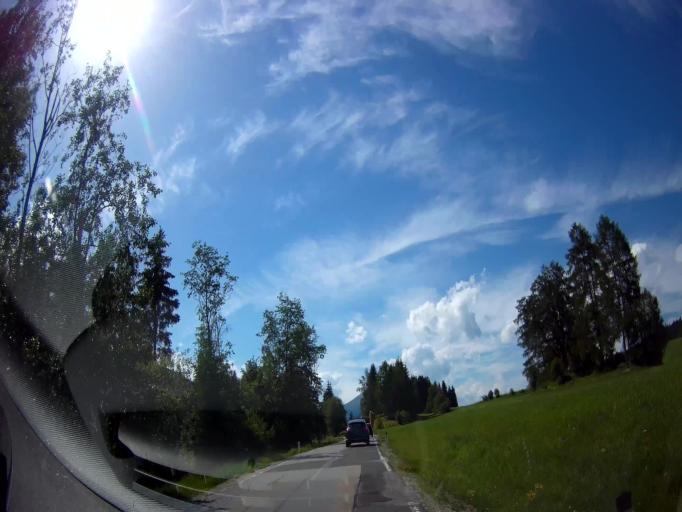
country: AT
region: Salzburg
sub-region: Politischer Bezirk Tamsweg
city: Thomatal
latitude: 47.0803
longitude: 13.7267
